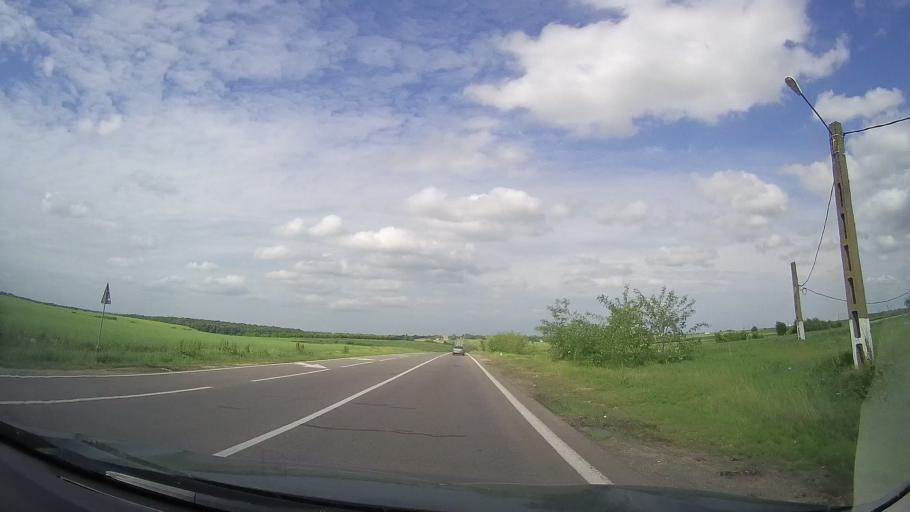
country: RO
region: Giurgiu
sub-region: Comuna Rasuceni
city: Rasuceni
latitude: 44.1196
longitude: 25.6644
